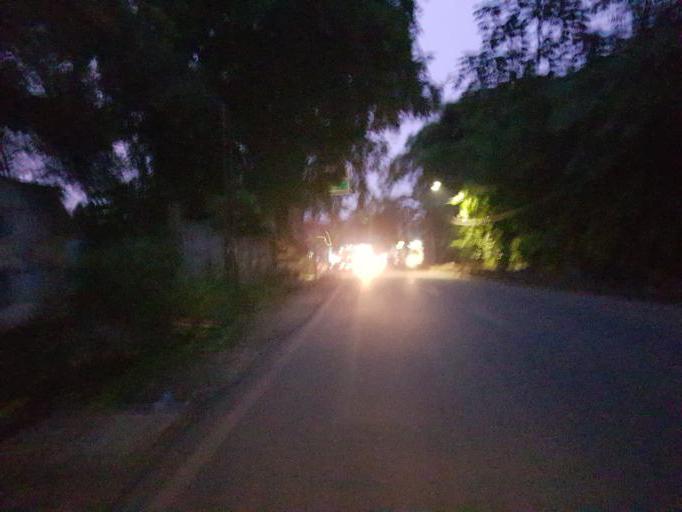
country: ID
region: West Java
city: Serpong
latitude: -6.3135
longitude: 106.6605
